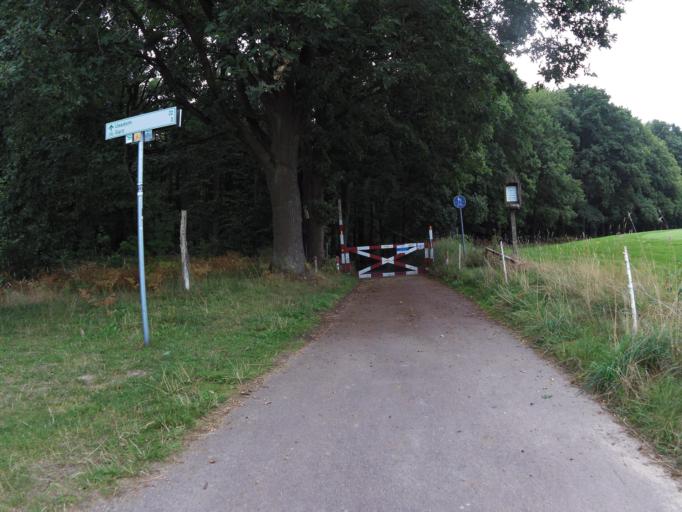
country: DE
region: Mecklenburg-Vorpommern
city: Seebad Heringsdorf
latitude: 53.9101
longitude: 14.1631
